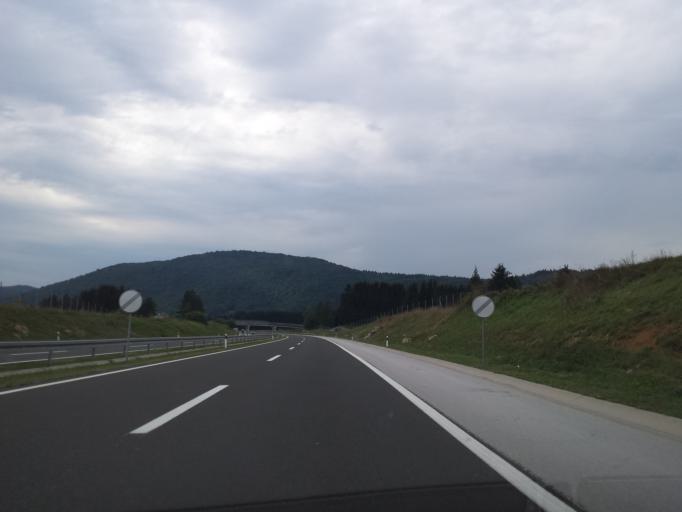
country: HR
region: Karlovacka
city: Ostarije
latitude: 45.2241
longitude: 15.2621
